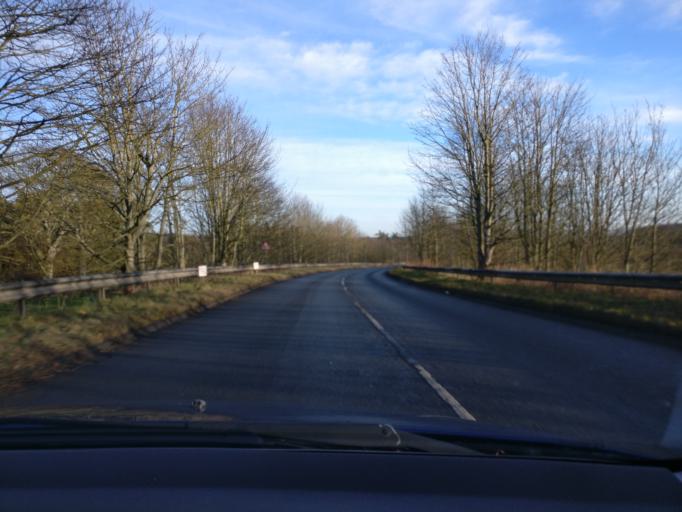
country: GB
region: Scotland
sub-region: The Scottish Borders
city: Jedburgh
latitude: 55.5075
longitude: -2.5412
